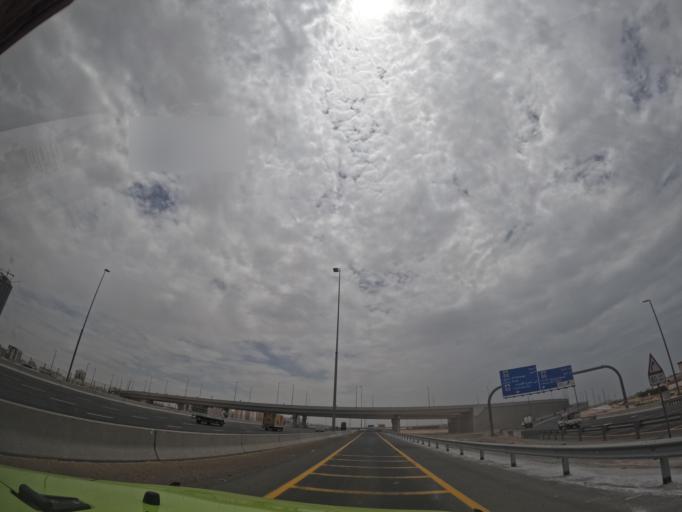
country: AE
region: Dubai
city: Dubai
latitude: 25.1234
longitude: 55.3676
